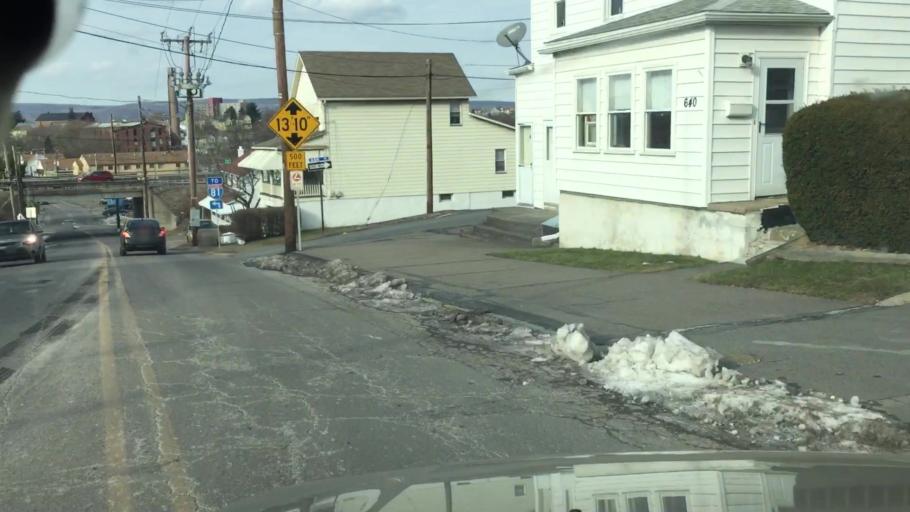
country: US
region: Pennsylvania
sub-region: Luzerne County
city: Georgetown
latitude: 41.2299
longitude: -75.8705
